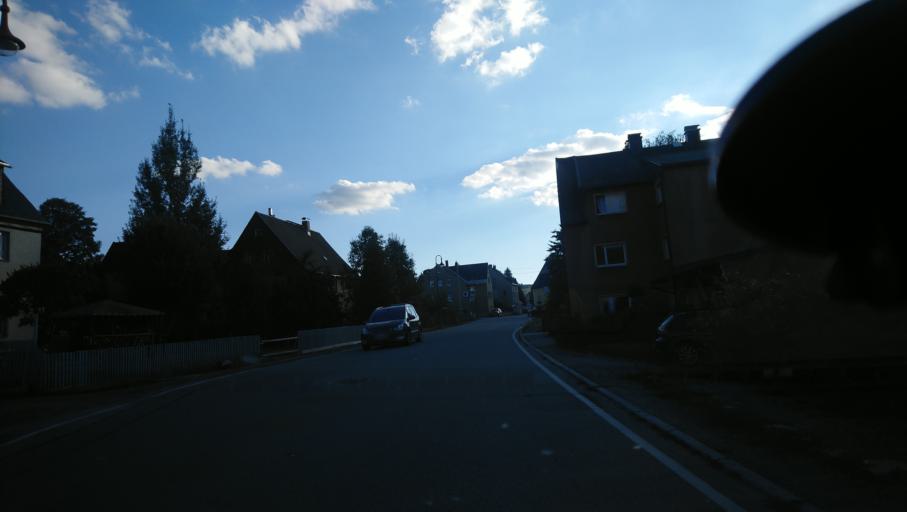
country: DE
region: Saxony
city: Crottendorf
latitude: 50.5157
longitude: 12.9454
